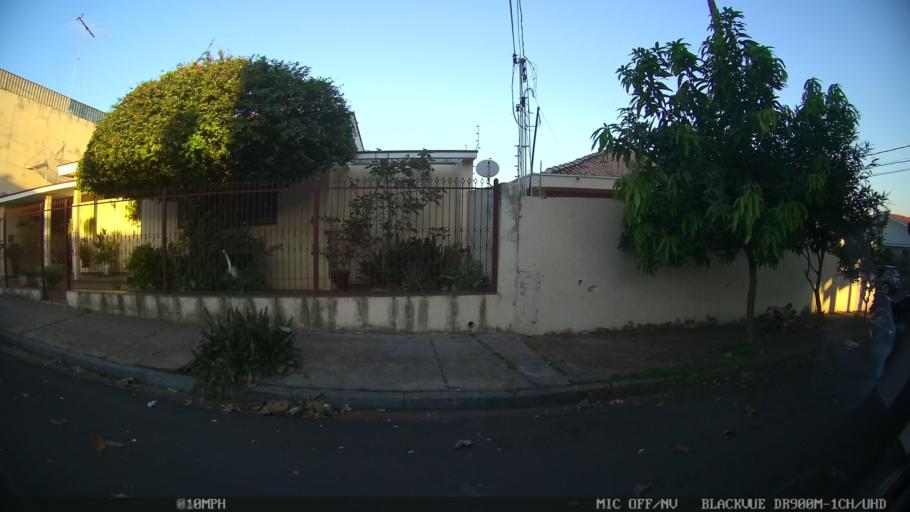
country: BR
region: Sao Paulo
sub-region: Sao Jose Do Rio Preto
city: Sao Jose do Rio Preto
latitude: -20.8035
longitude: -49.3684
